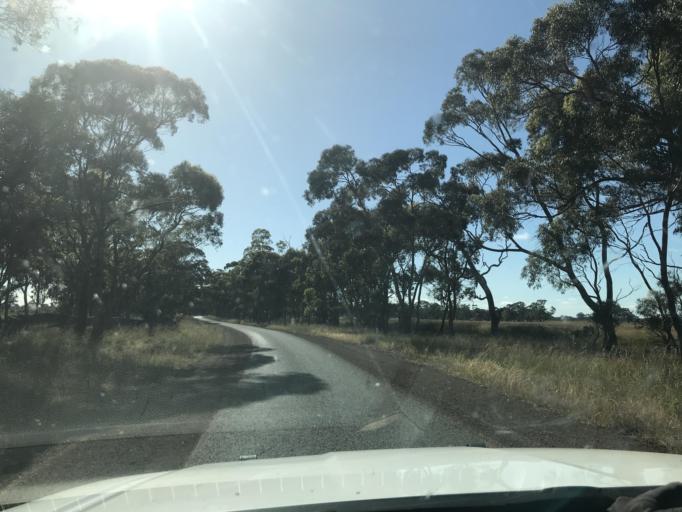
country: AU
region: Victoria
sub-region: Horsham
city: Horsham
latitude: -37.0261
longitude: 141.7128
